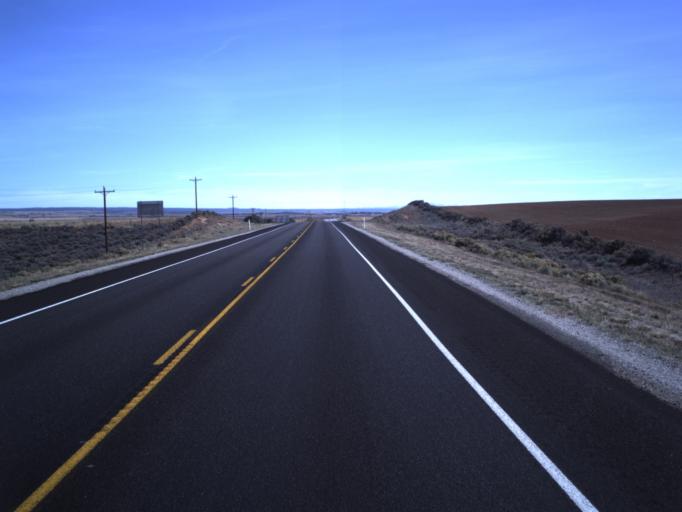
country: US
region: Colorado
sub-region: Dolores County
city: Dove Creek
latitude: 37.8180
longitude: -109.0473
